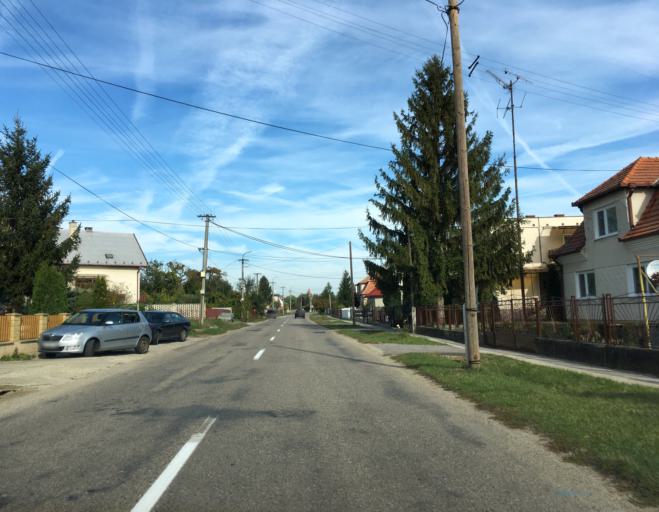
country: SK
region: Nitriansky
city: Svodin
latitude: 48.0103
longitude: 18.4139
